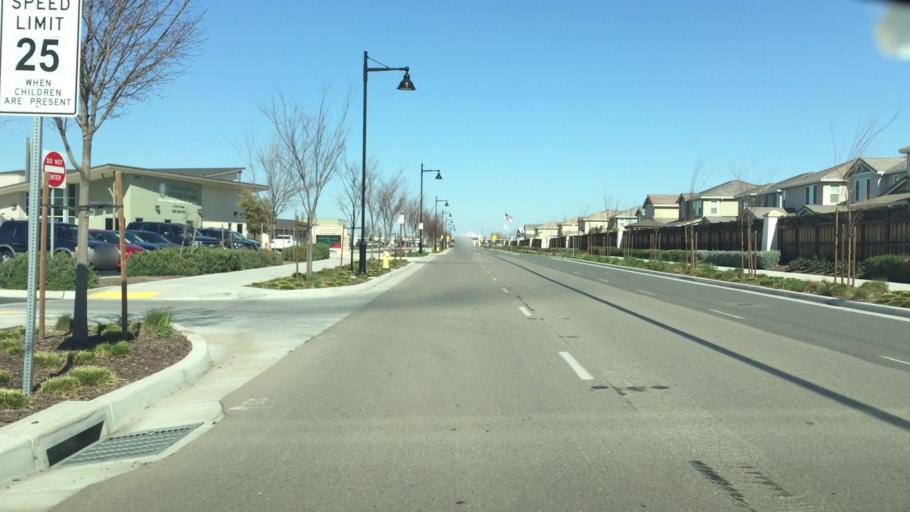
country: US
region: California
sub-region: San Joaquin County
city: Lathrop
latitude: 37.7956
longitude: -121.3185
